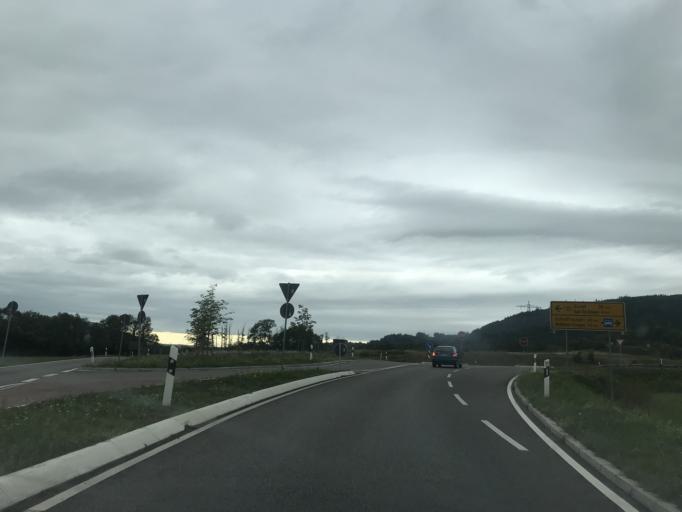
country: CH
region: Aargau
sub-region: Bezirk Laufenburg
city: Eiken
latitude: 47.5586
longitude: 7.9942
